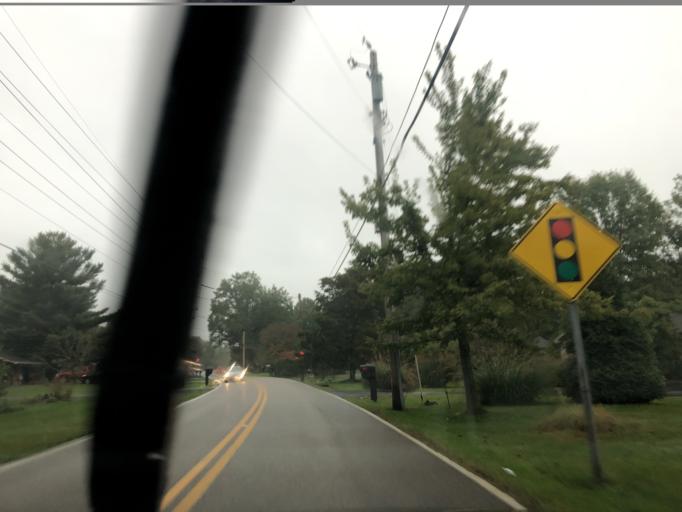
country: US
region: Ohio
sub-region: Clermont County
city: Mulberry
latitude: 39.2132
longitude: -84.2431
